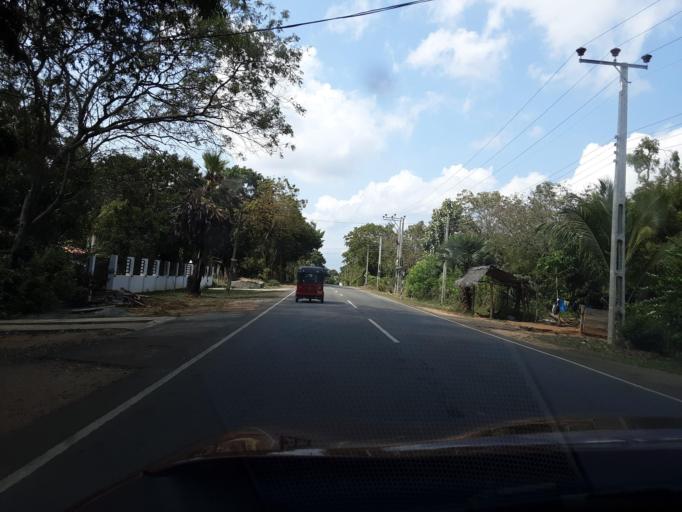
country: LK
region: Southern
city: Tangalla
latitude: 6.2661
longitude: 81.2260
